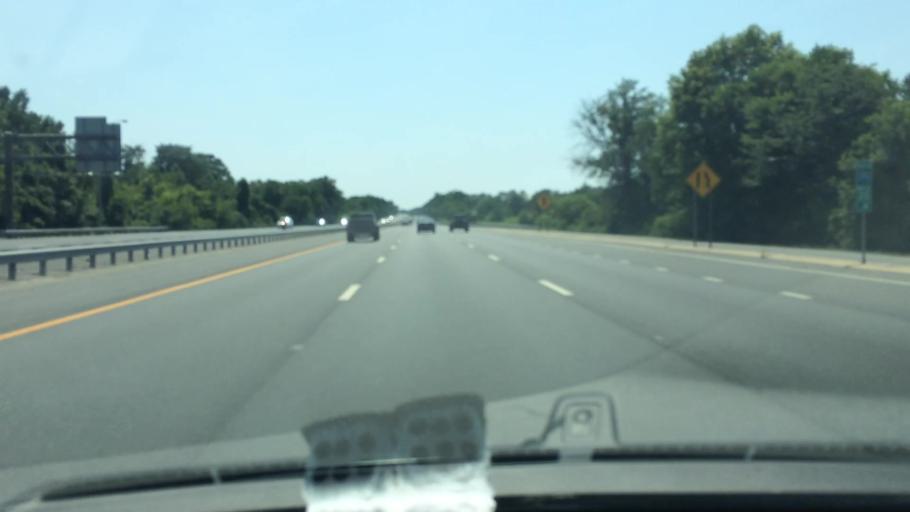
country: US
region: New Jersey
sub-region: Gloucester County
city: Paulsboro
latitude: 39.8359
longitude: -75.2048
